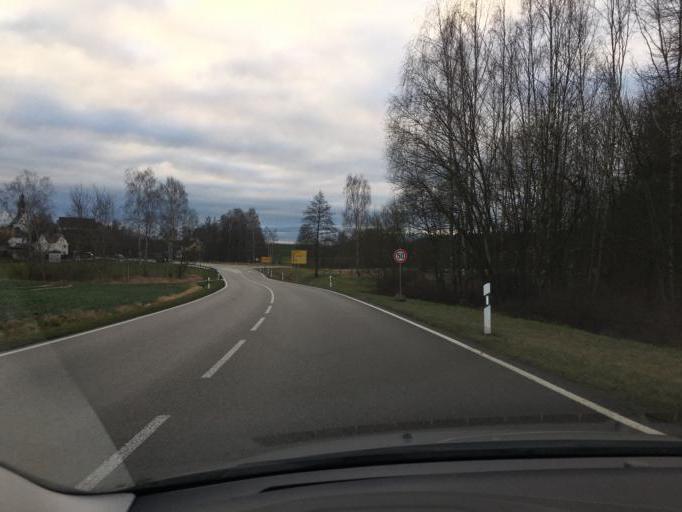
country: DE
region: Thuringia
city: Langenleuba-Niederhain
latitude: 50.9954
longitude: 12.5648
